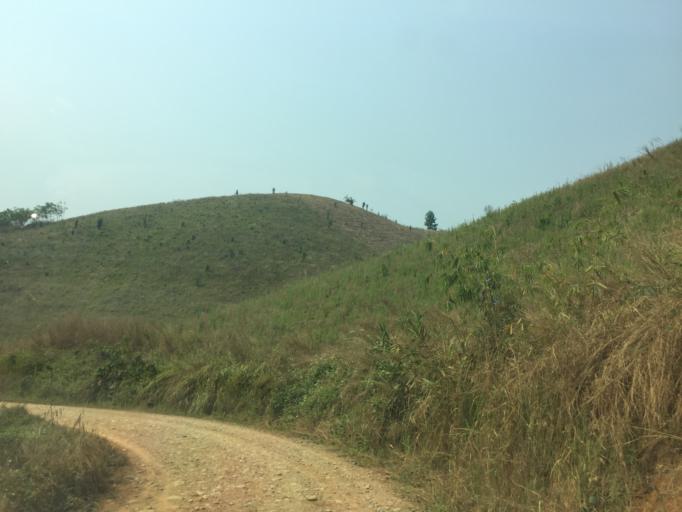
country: TH
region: Phayao
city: Phu Sang
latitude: 19.5860
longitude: 100.5256
